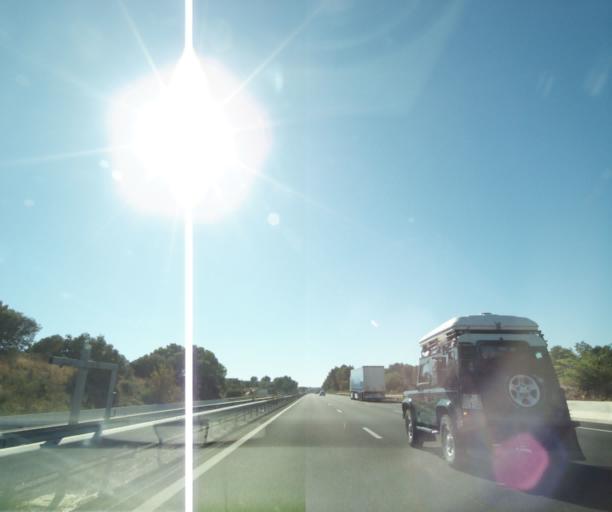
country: FR
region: Languedoc-Roussillon
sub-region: Departement de l'Herault
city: Fabregues
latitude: 43.5303
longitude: 3.7735
